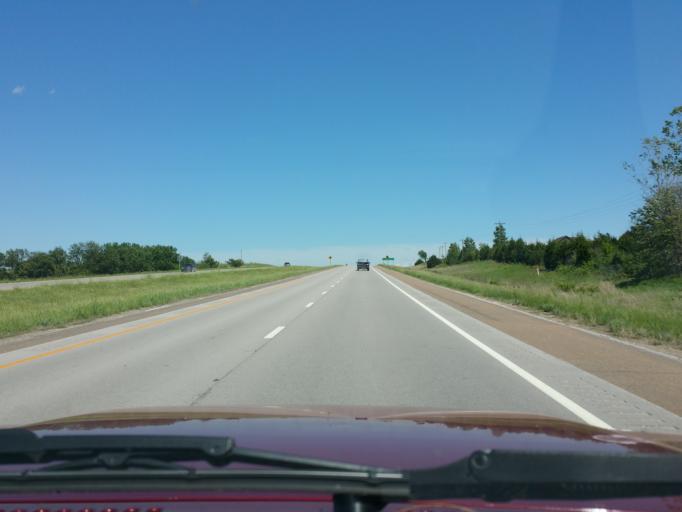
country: US
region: Kansas
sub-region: Pottawatomie County
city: Wamego
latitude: 39.2099
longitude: -96.3947
